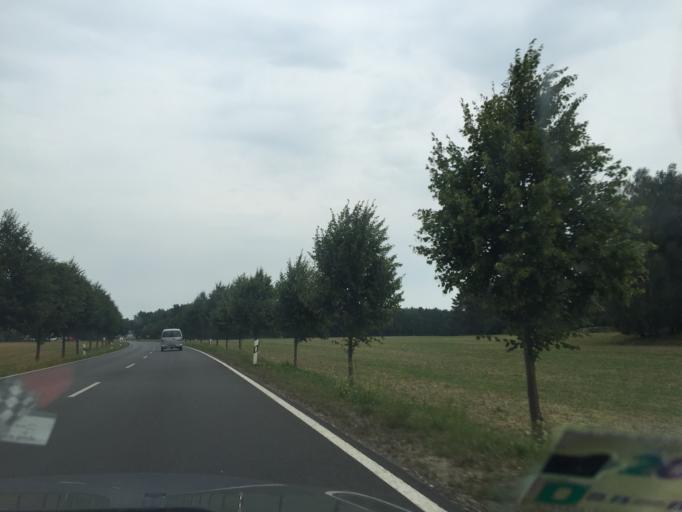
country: DE
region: Brandenburg
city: Wandlitz
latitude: 52.7429
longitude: 13.4483
